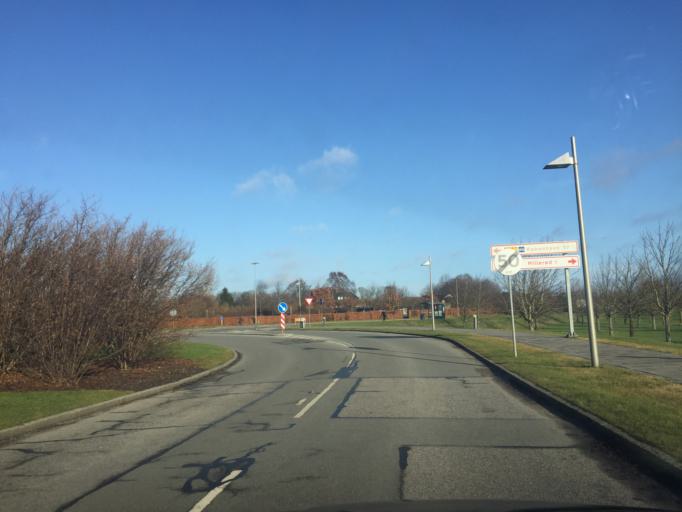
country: DK
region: Capital Region
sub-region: Hillerod Kommune
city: Hillerod
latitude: 55.9183
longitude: 12.2850
